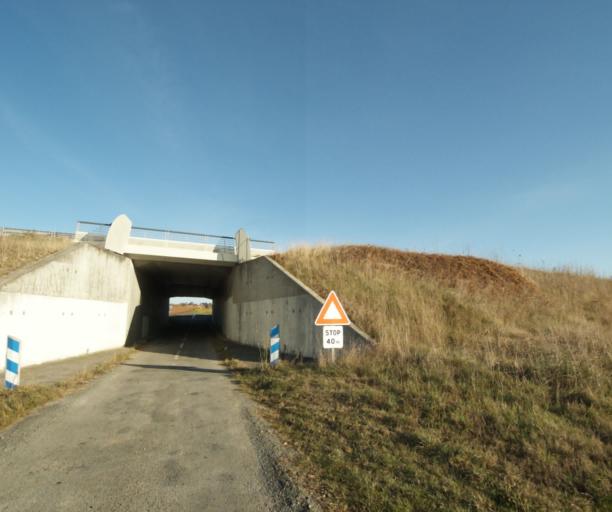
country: FR
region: Poitou-Charentes
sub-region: Departement de la Charente-Maritime
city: Cherac
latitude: 45.6985
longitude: -0.4549
